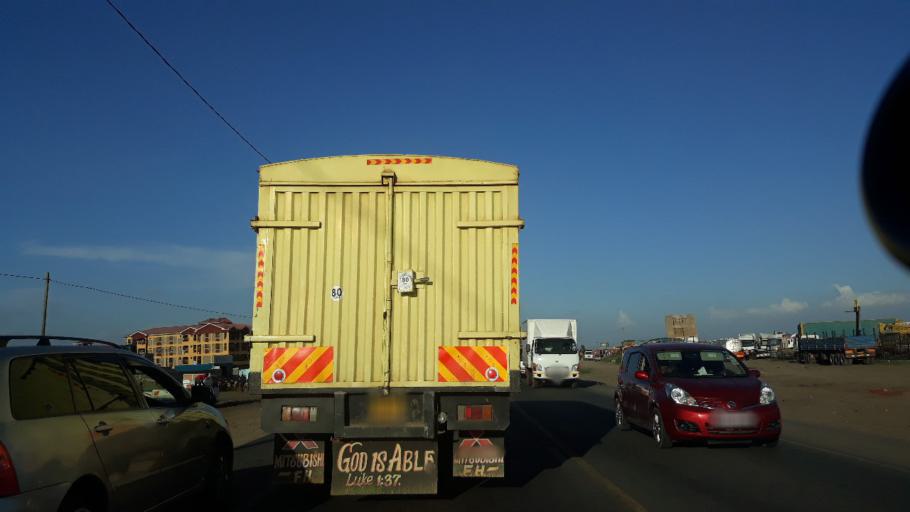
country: KE
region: Nairobi Area
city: Pumwani
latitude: -1.2928
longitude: 36.9443
